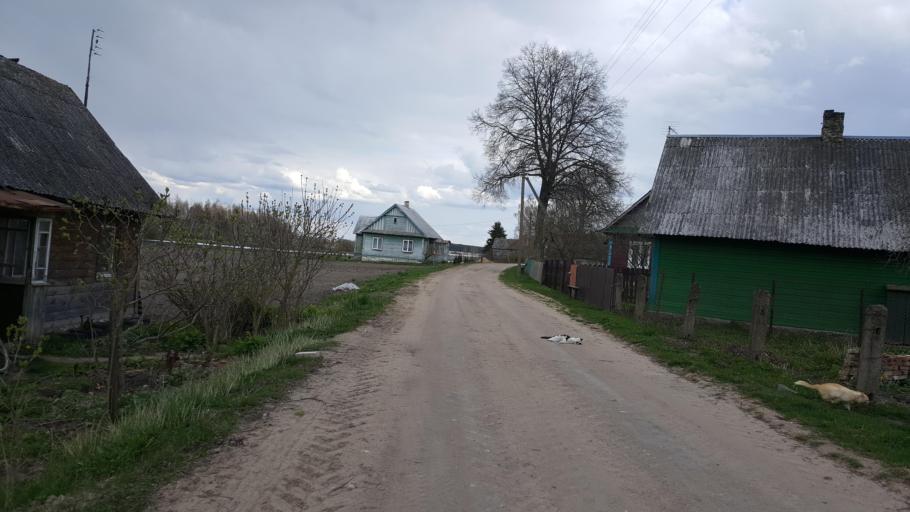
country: BY
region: Brest
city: Kamyanyets
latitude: 52.4064
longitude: 23.7156
